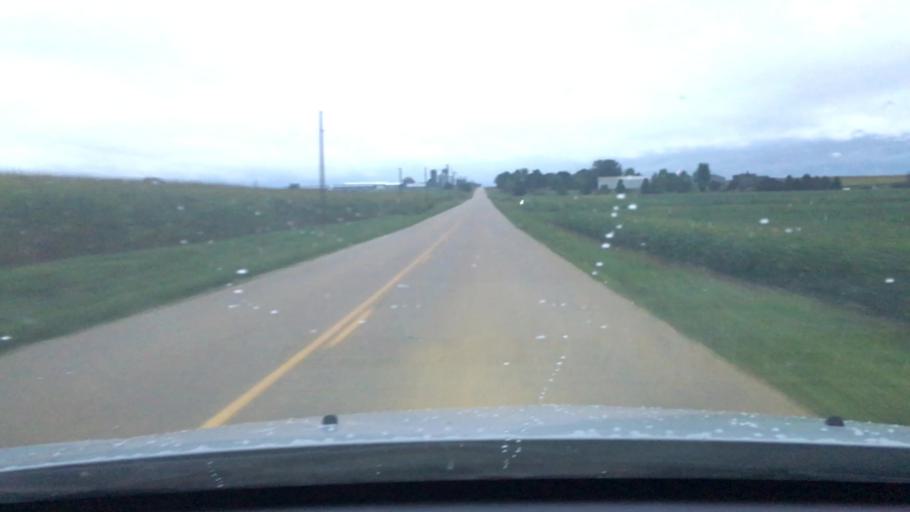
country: US
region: Illinois
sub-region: DeKalb County
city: Malta
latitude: 41.8608
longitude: -88.9614
